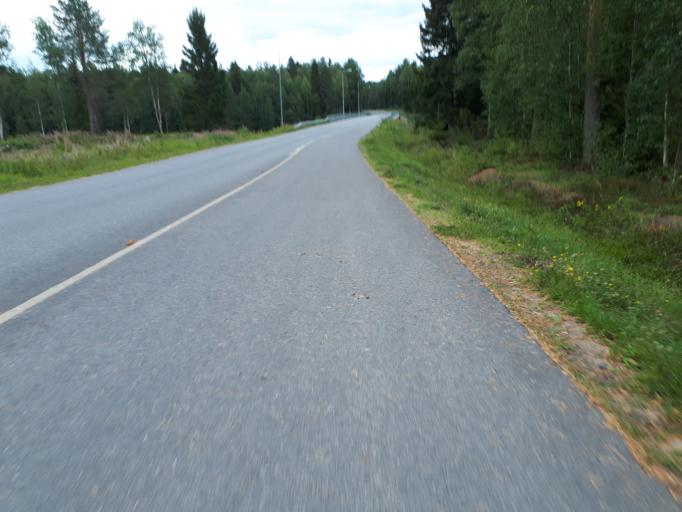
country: FI
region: Northern Ostrobothnia
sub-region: Oulunkaari
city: Ii
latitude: 65.3234
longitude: 25.4102
